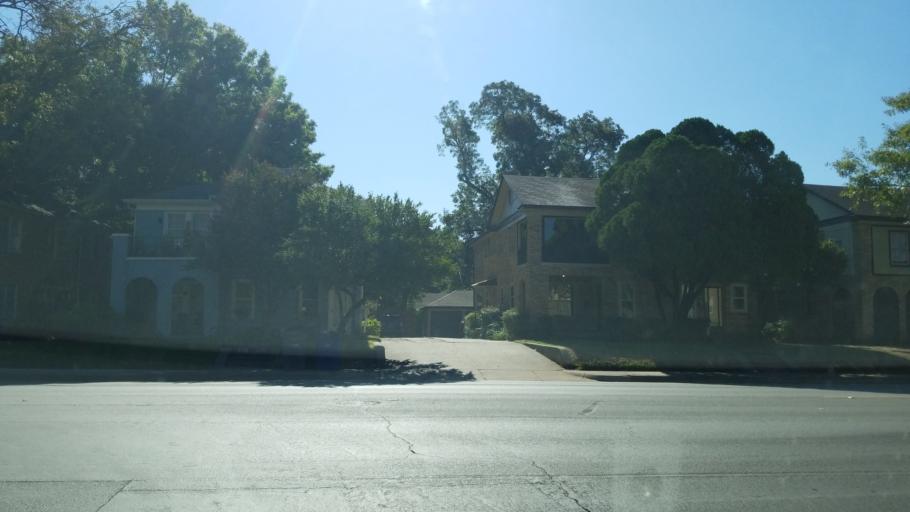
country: US
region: Texas
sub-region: Dallas County
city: Highland Park
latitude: 32.8111
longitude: -96.7629
